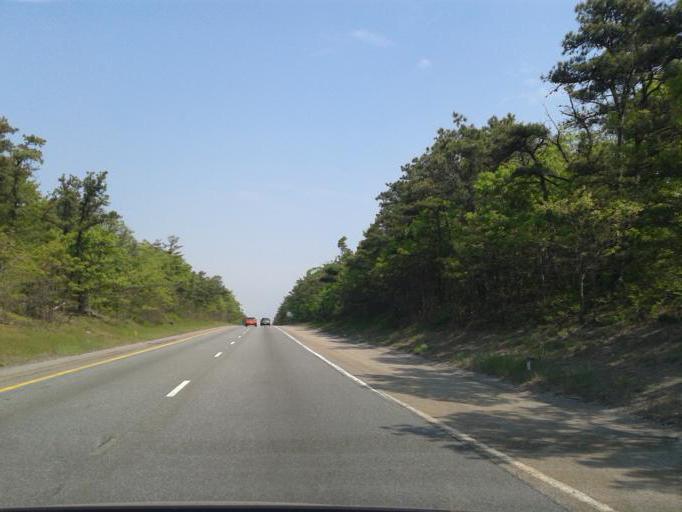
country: US
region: Massachusetts
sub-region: Barnstable County
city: Sagamore
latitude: 41.8195
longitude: -70.5563
